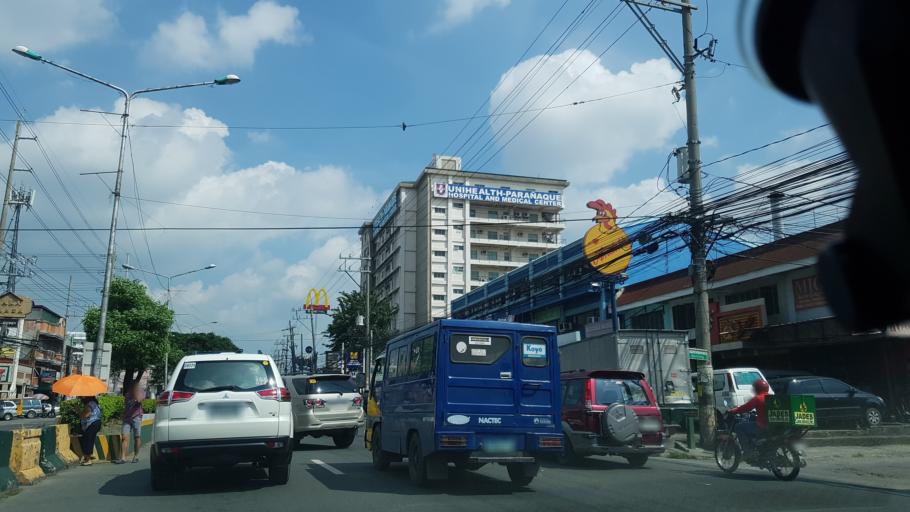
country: PH
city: Sambayanihan People's Village
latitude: 14.4652
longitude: 121.0187
